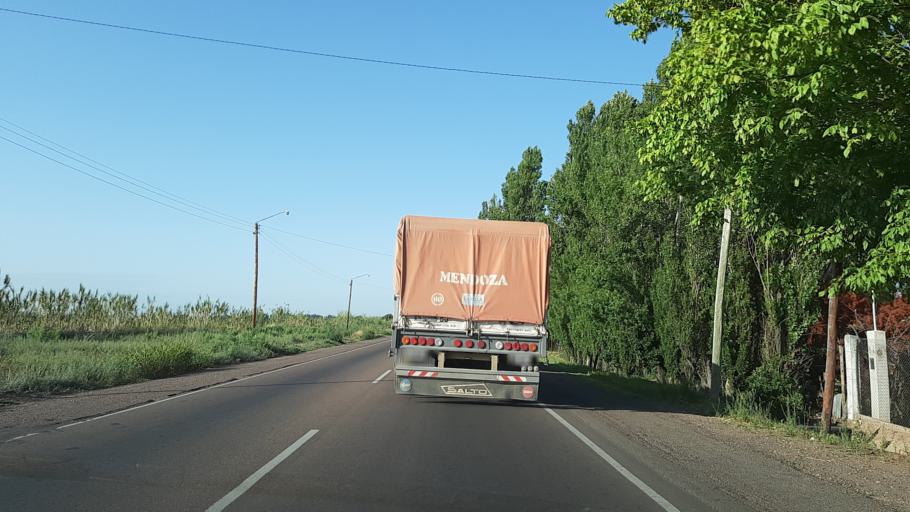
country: AR
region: Mendoza
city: San Martin
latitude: -32.9918
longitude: -68.4707
